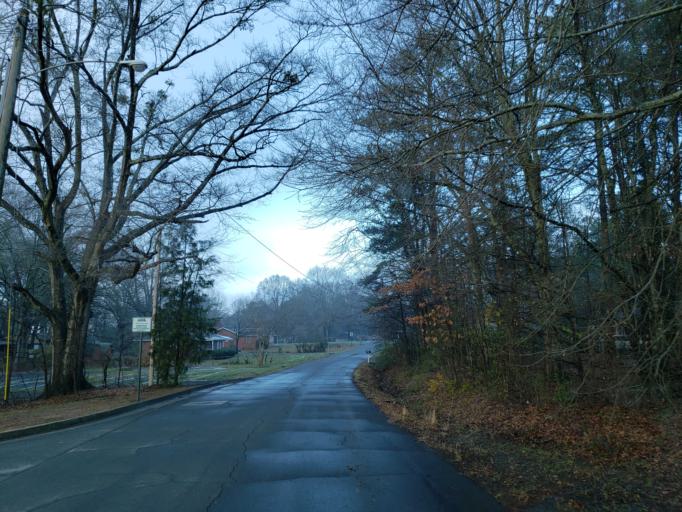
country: US
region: Georgia
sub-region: Cobb County
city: Kennesaw
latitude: 34.0249
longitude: -84.6135
